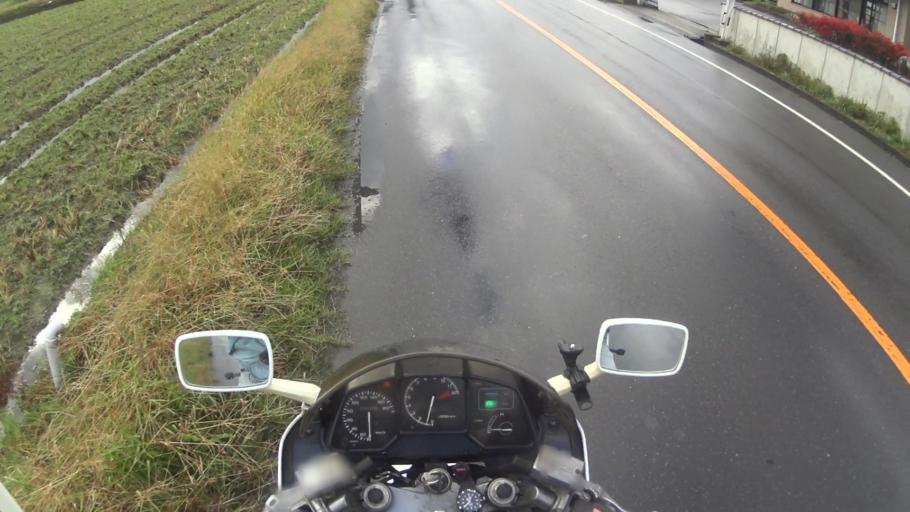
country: JP
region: Kyoto
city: Miyazu
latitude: 35.5530
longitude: 135.1598
